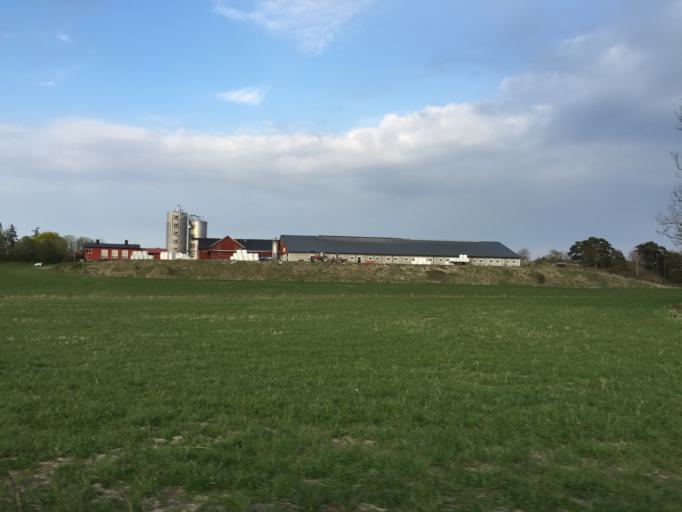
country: SE
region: Stockholm
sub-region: Sodertalje Kommun
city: Pershagen
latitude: 59.0727
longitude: 17.6050
